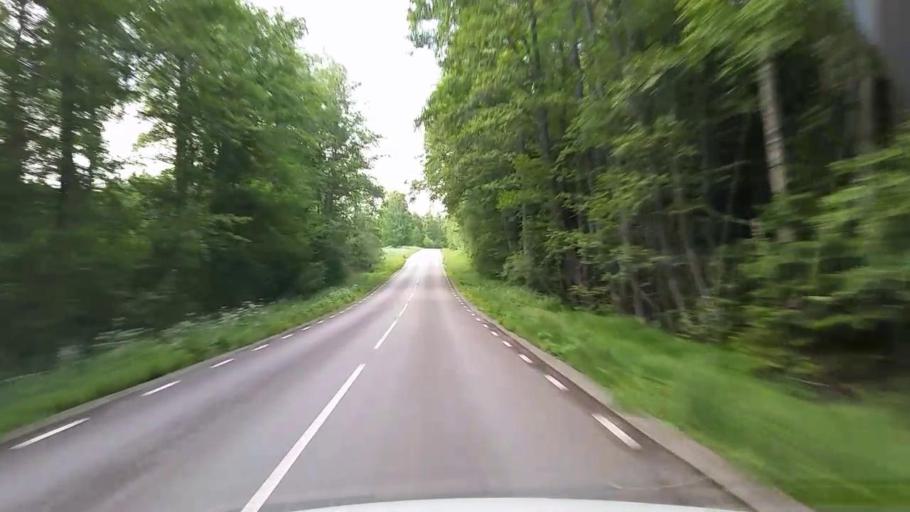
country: SE
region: Vaestmanland
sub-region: Kopings Kommun
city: Kolsva
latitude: 59.7569
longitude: 15.8346
